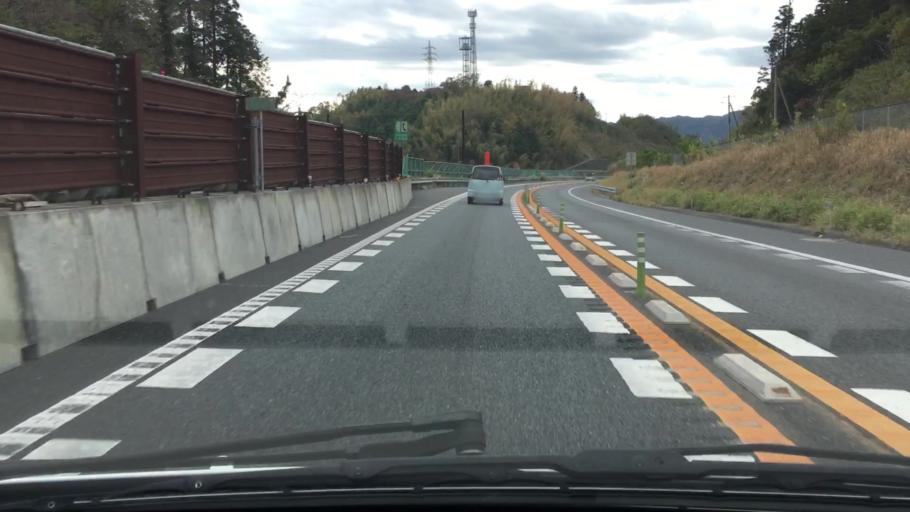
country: JP
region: Chiba
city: Kimitsu
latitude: 35.2302
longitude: 139.8868
